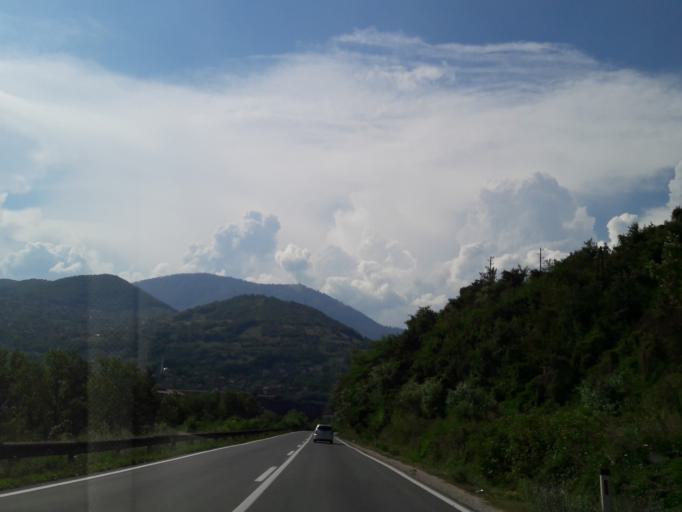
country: BA
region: Federation of Bosnia and Herzegovina
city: Zenica
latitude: 44.2341
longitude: 17.9016
